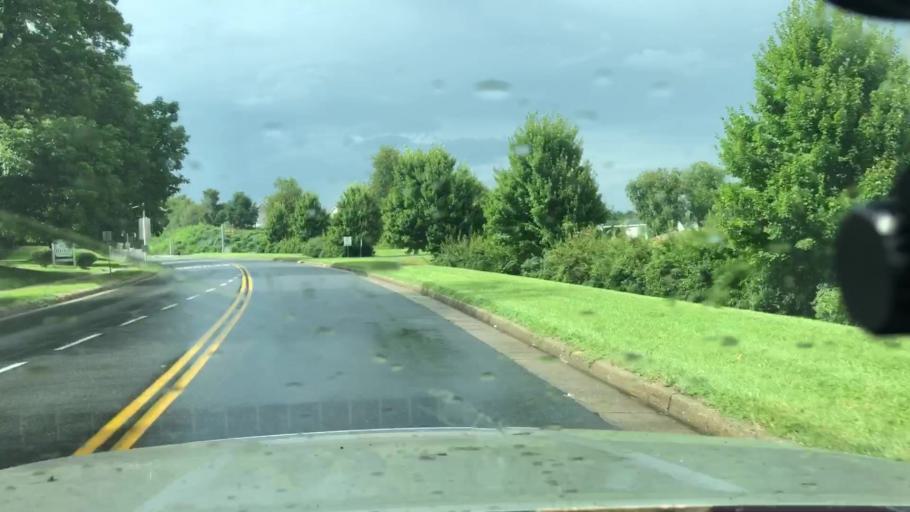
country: US
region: Virginia
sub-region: City of Waynesboro
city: Waynesboro
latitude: 38.0809
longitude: -78.8966
